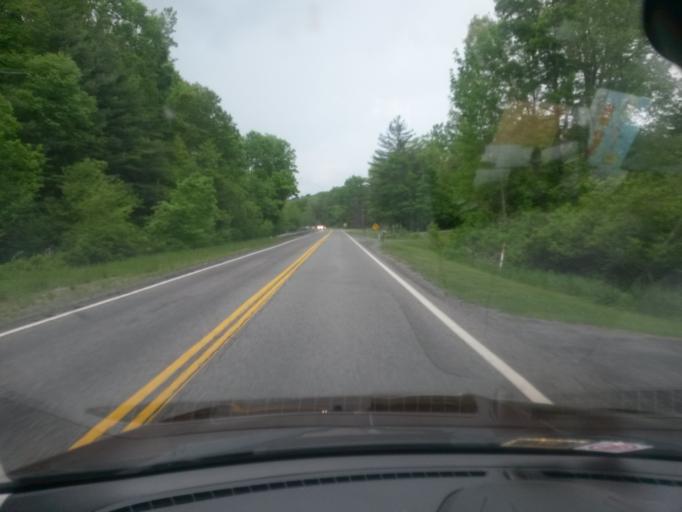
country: US
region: Virginia
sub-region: Floyd County
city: Floyd
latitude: 36.9574
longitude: -80.3676
